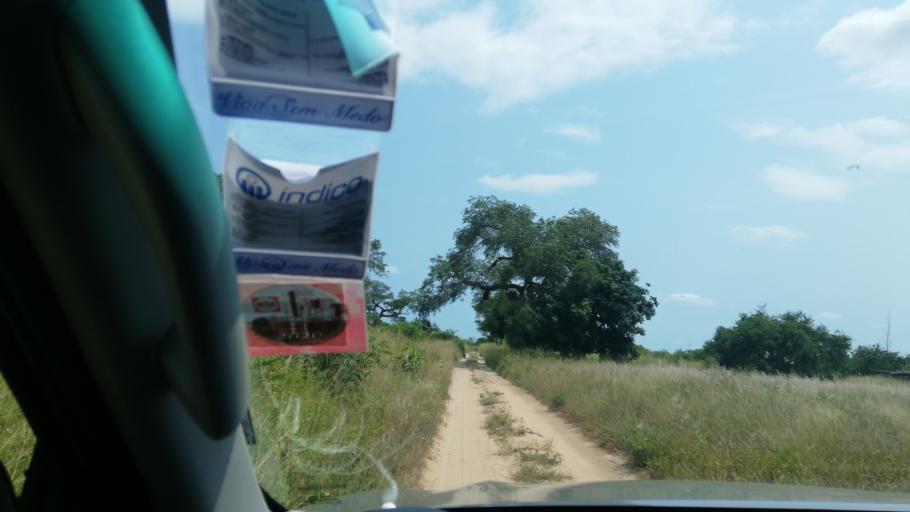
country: MZ
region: Maputo
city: Matola
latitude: -26.1101
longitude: 32.4248
